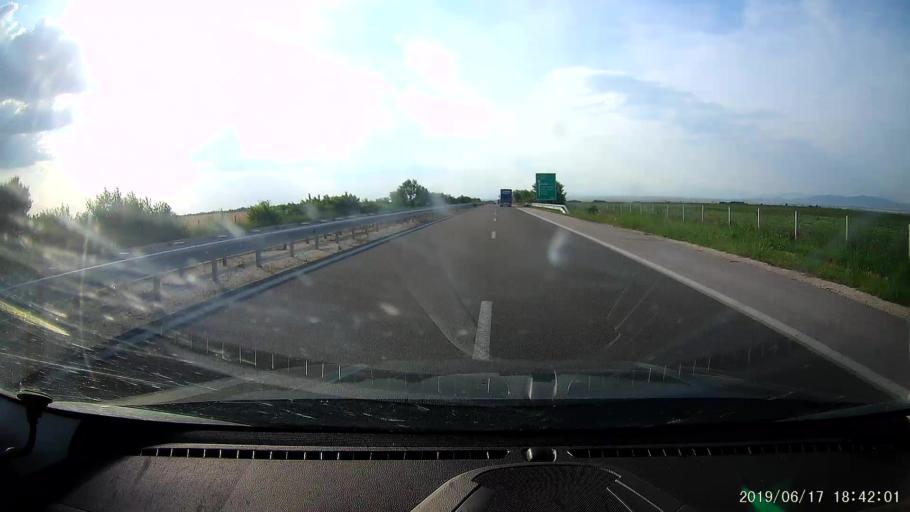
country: BG
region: Stara Zagora
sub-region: Obshtina Chirpan
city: Chirpan
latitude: 42.1833
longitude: 25.2449
